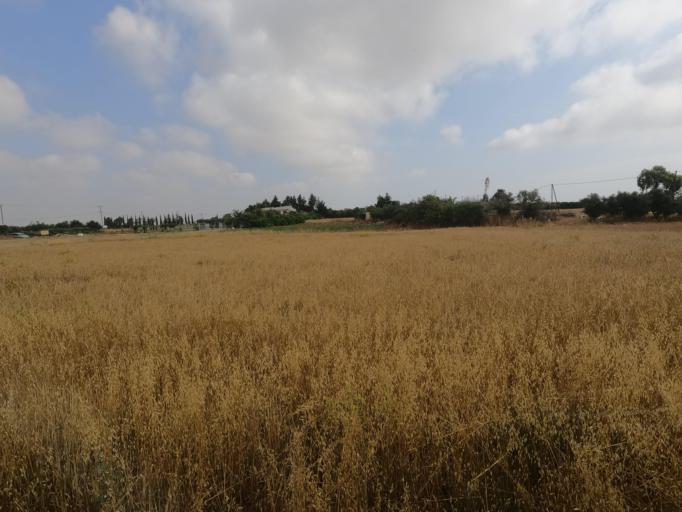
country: CY
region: Ammochostos
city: Deryneia
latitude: 35.0592
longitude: 33.9418
